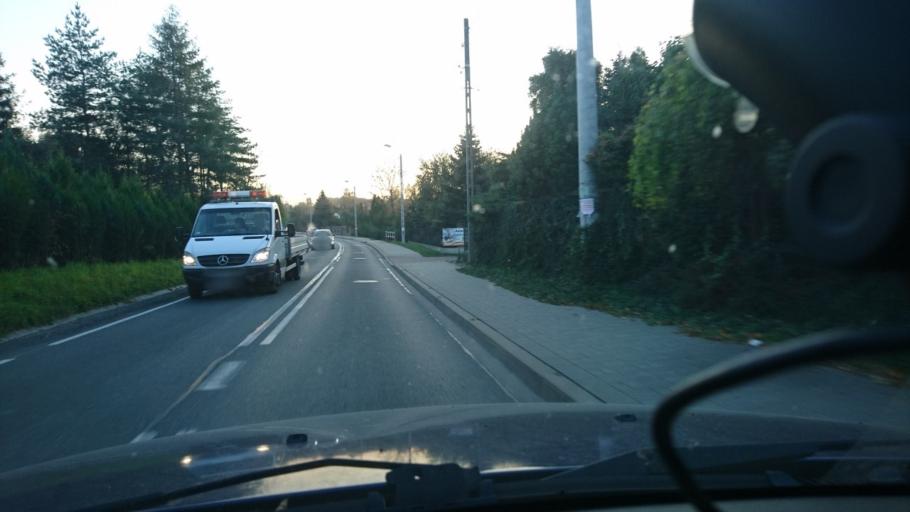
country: PL
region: Silesian Voivodeship
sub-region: Powiat bielski
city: Kozy
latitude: 49.8536
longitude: 19.1372
